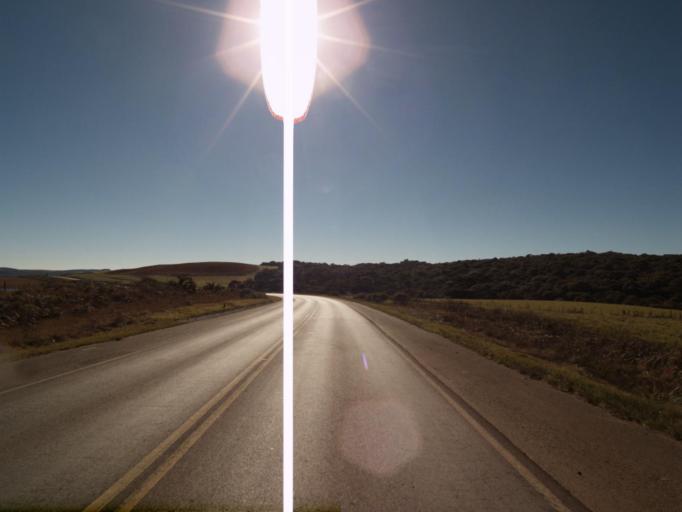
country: BR
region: Santa Catarina
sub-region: Joacaba
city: Joacaba
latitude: -26.7915
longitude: -51.6896
